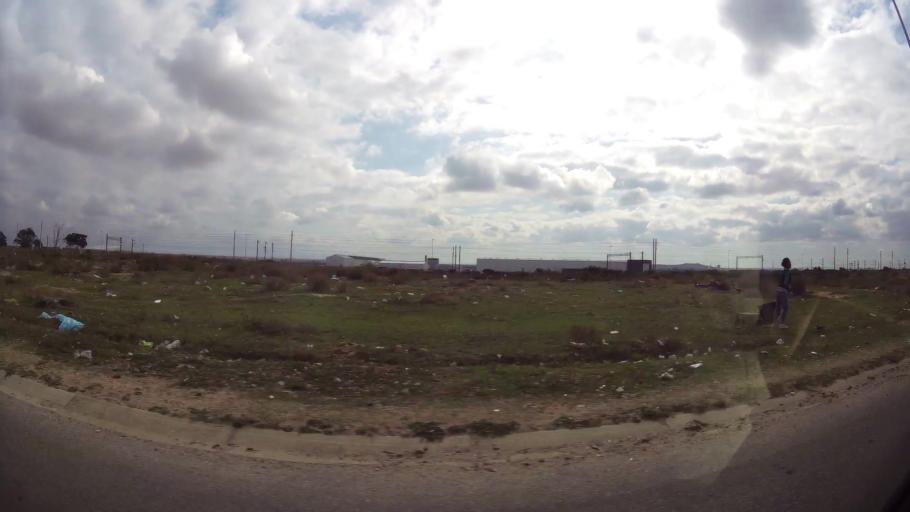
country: ZA
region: Eastern Cape
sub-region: Nelson Mandela Bay Metropolitan Municipality
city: Port Elizabeth
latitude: -33.8180
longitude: 25.6309
